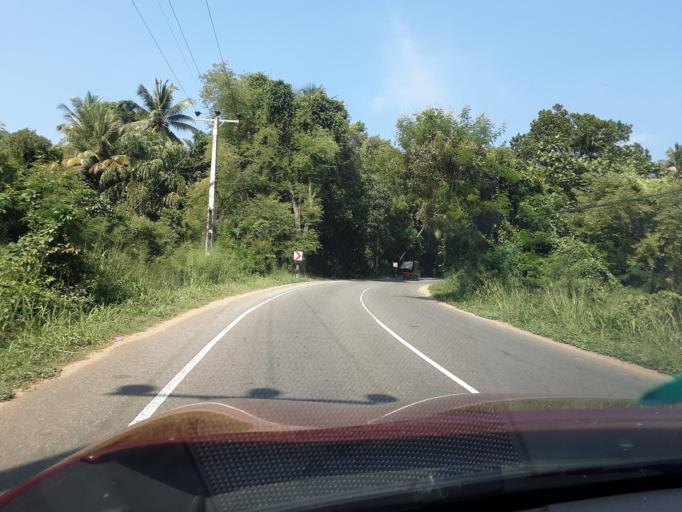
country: LK
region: Uva
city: Badulla
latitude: 7.1965
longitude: 81.0196
